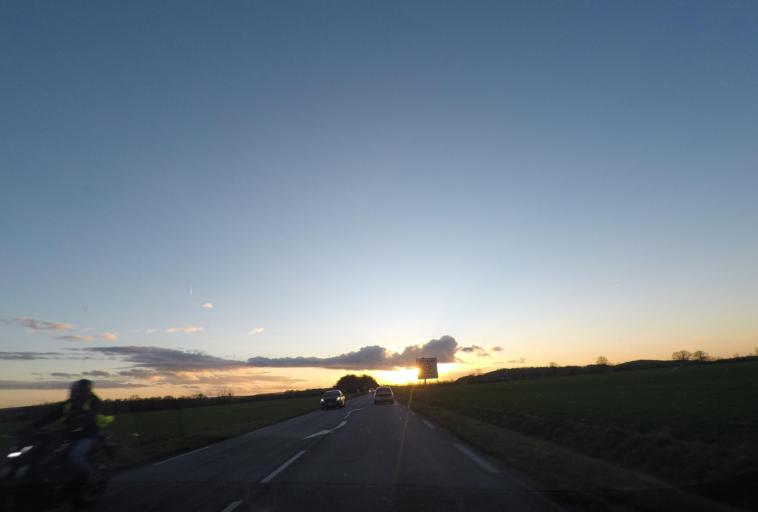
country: FR
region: Ile-de-France
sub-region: Departement de l'Essonne
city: Lisses
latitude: 48.5830
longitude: 2.4220
